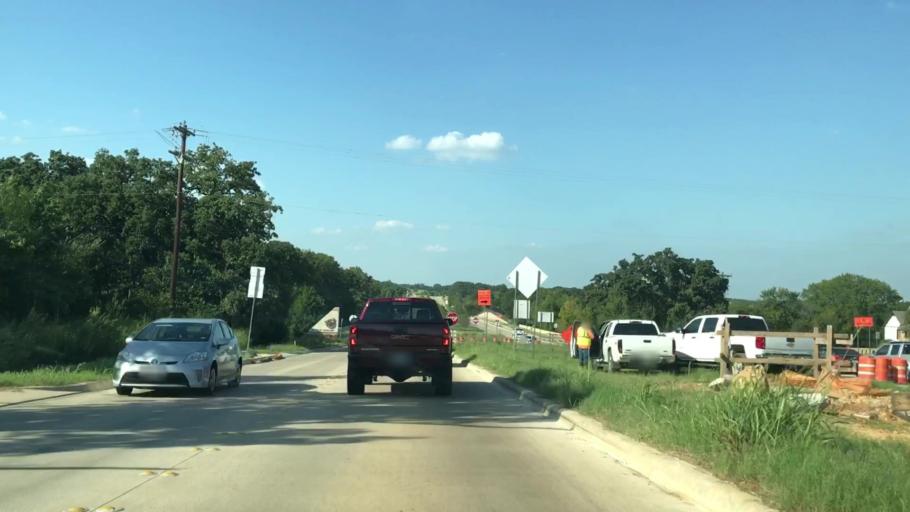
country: US
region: Texas
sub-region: Denton County
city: Trophy Club
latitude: 32.9598
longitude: -97.1860
